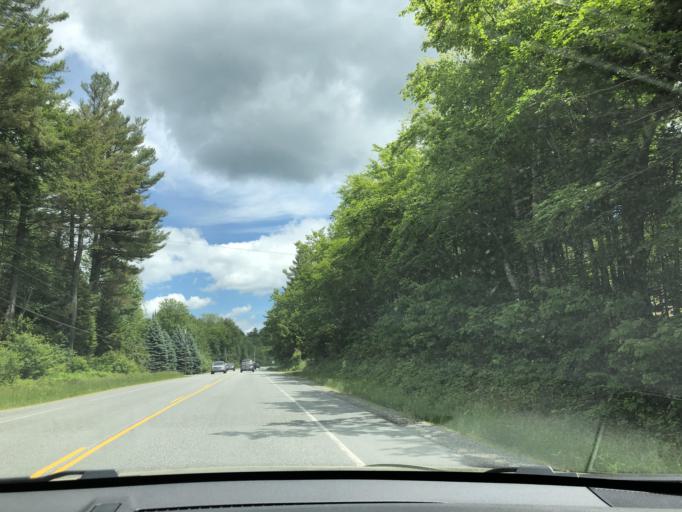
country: US
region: New Hampshire
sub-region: Merrimack County
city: New London
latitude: 43.4267
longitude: -72.0132
